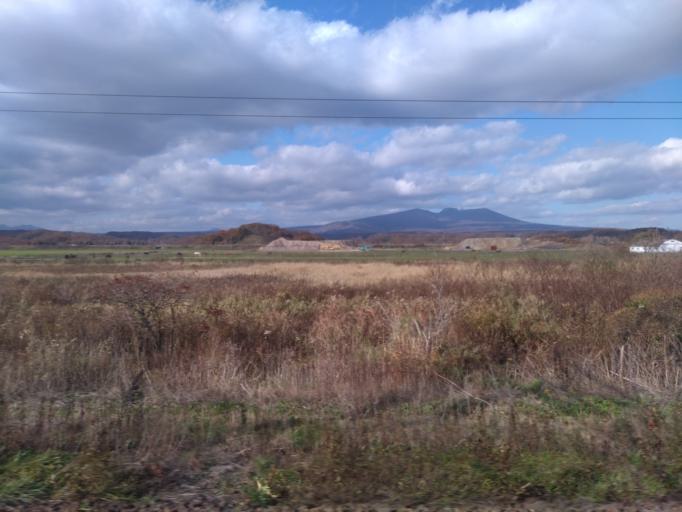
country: JP
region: Hokkaido
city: Shiraoi
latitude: 42.5770
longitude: 141.4119
